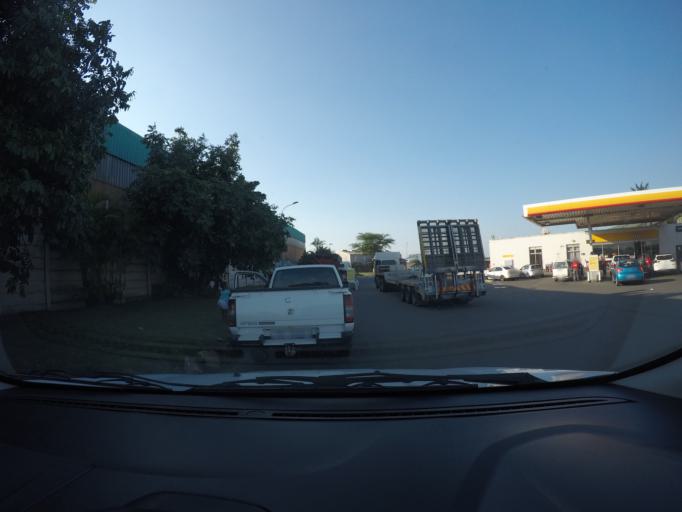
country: ZA
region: KwaZulu-Natal
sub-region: uThungulu District Municipality
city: Richards Bay
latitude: -28.7525
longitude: 32.0273
